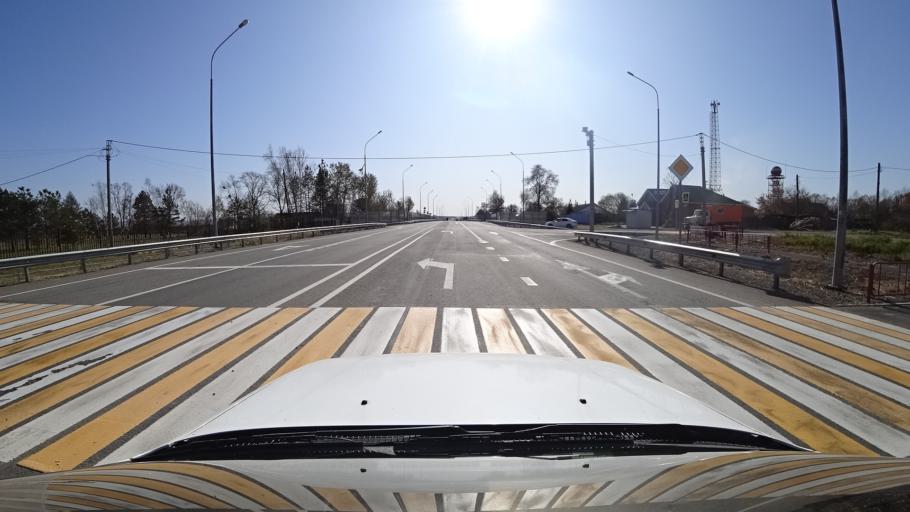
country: RU
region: Primorskiy
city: Dal'nerechensk
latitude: 45.8809
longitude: 133.7284
